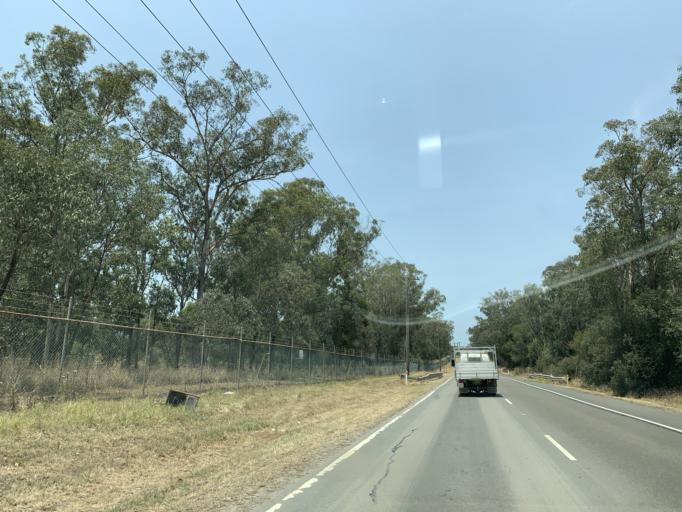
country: AU
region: New South Wales
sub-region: Fairfield
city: Horsley Park
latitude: -33.8259
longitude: 150.8716
